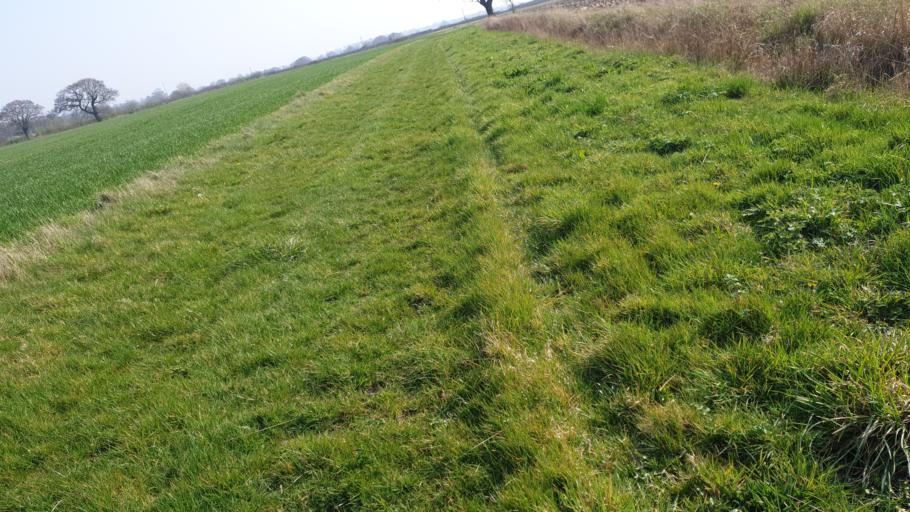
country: GB
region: England
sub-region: Essex
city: Mistley
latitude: 51.9043
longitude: 1.1284
